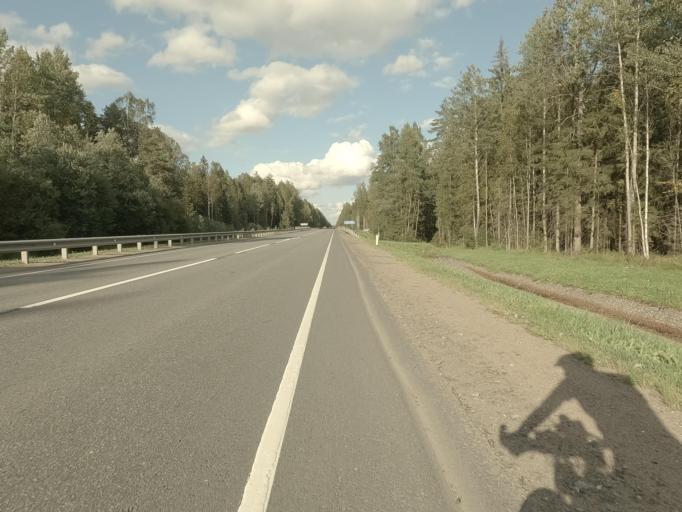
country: RU
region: Leningrad
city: Mga
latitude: 59.6945
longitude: 30.9839
